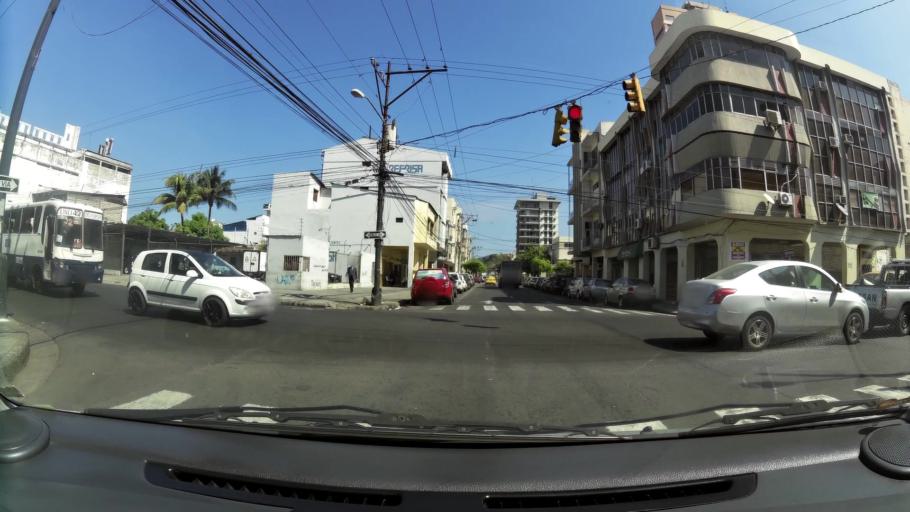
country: EC
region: Guayas
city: Guayaquil
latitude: -2.1891
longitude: -79.8928
